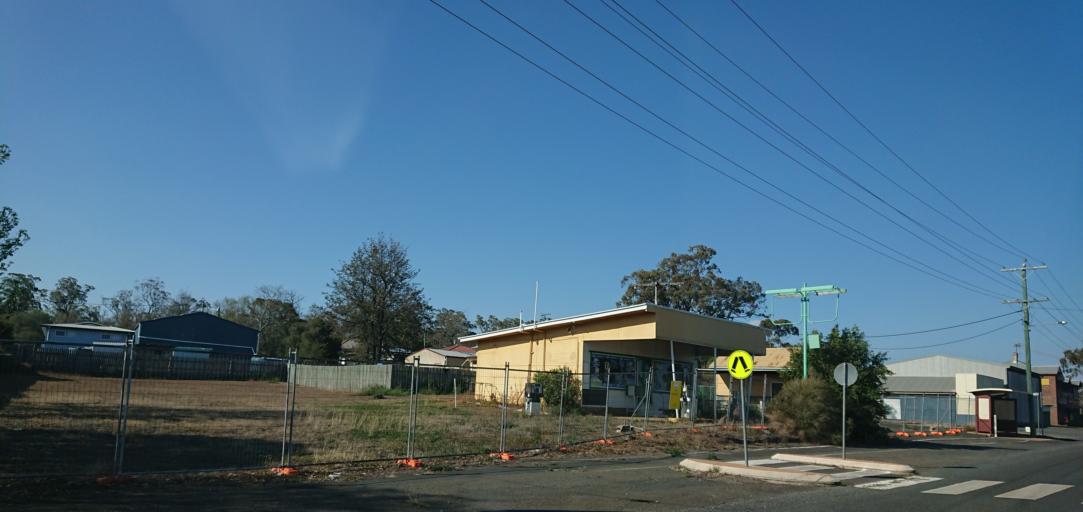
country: AU
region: Queensland
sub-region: Toowoomba
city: Westbrook
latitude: -27.6786
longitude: 151.7129
